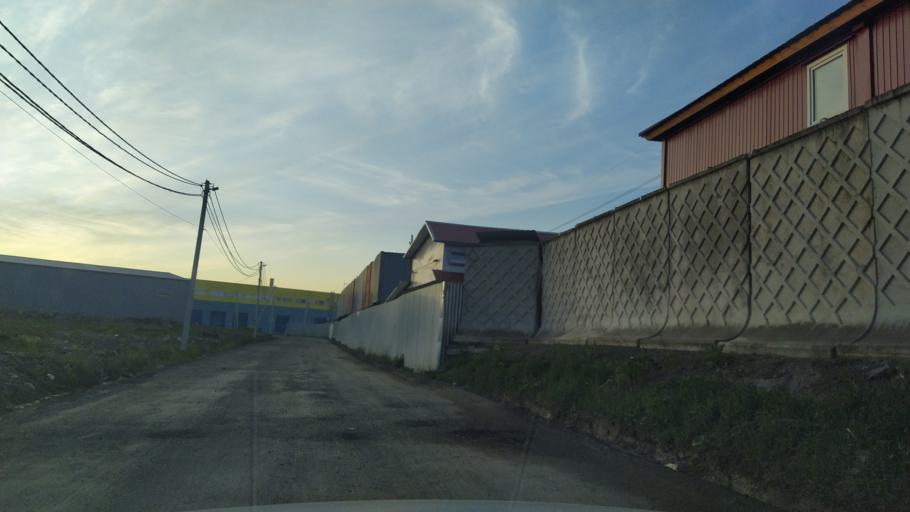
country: RU
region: St.-Petersburg
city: Obukhovo
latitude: 59.8049
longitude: 30.4596
